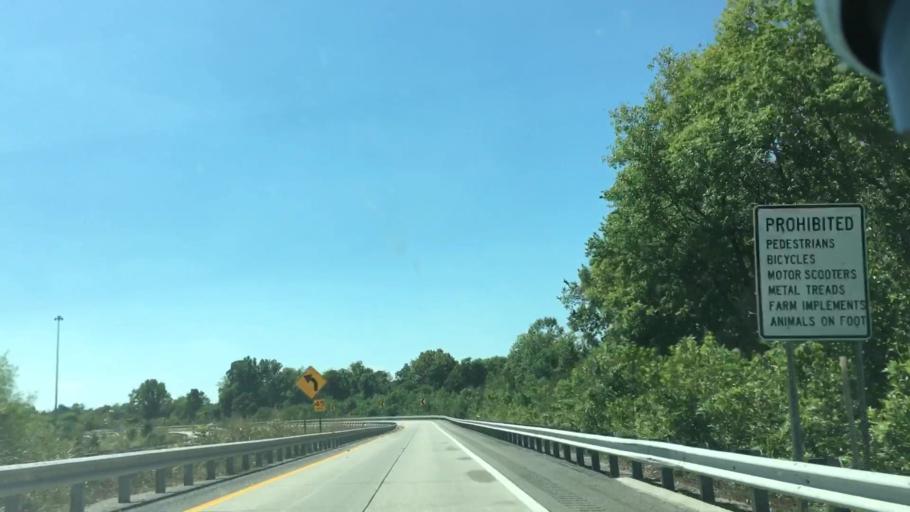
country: US
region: Kentucky
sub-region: Henderson County
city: Henderson
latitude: 37.8135
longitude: -87.5649
